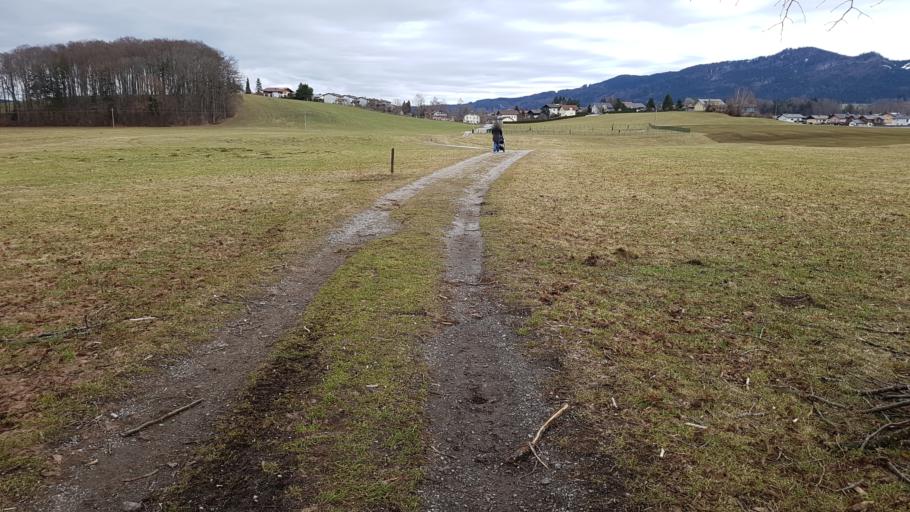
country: AT
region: Salzburg
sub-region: Politischer Bezirk Salzburg-Umgebung
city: Henndorf am Wallersee
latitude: 47.8971
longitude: 13.1726
